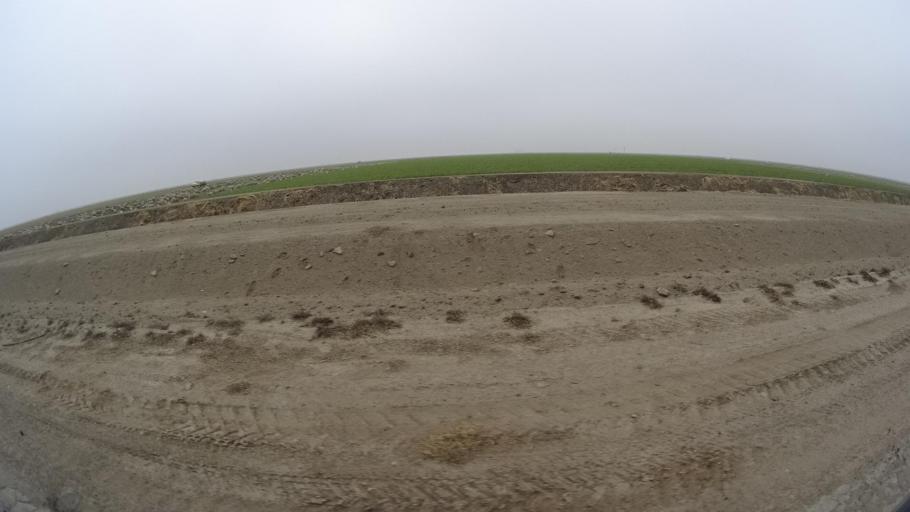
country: US
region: California
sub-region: Kern County
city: Rosedale
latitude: 35.1917
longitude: -119.1991
